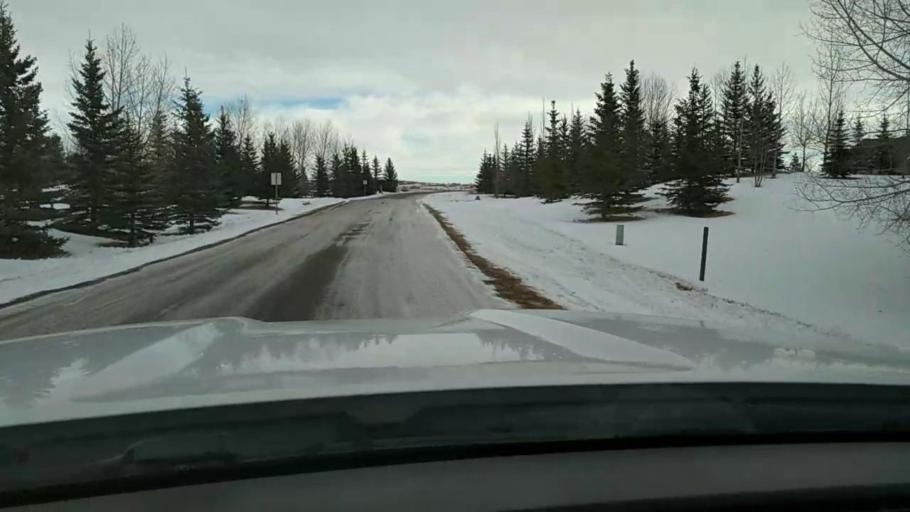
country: CA
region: Alberta
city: Cochrane
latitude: 51.2090
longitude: -114.2830
